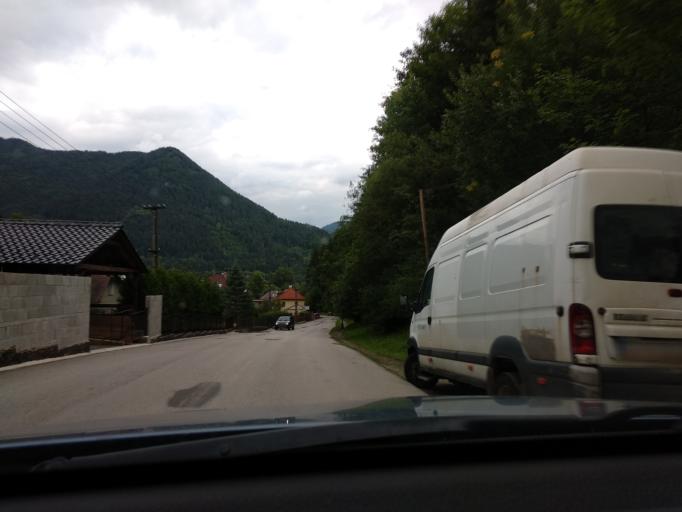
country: SK
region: Zilinsky
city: Ruzomberok
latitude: 49.0785
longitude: 19.2784
